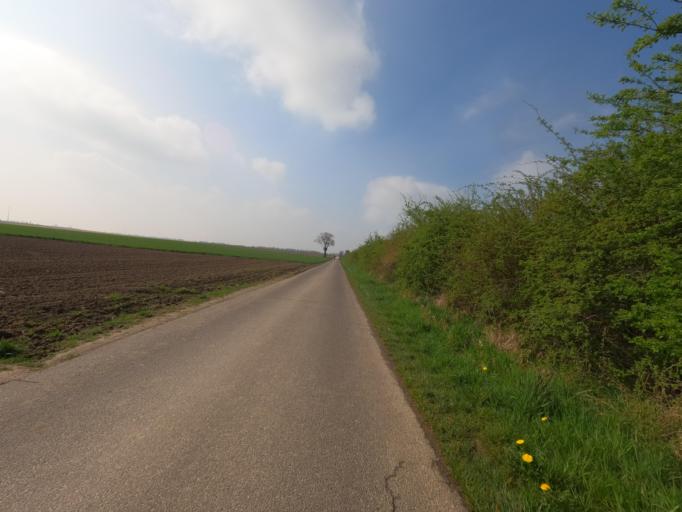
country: DE
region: North Rhine-Westphalia
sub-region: Regierungsbezirk Koln
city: Heinsberg
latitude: 51.0463
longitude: 6.0810
